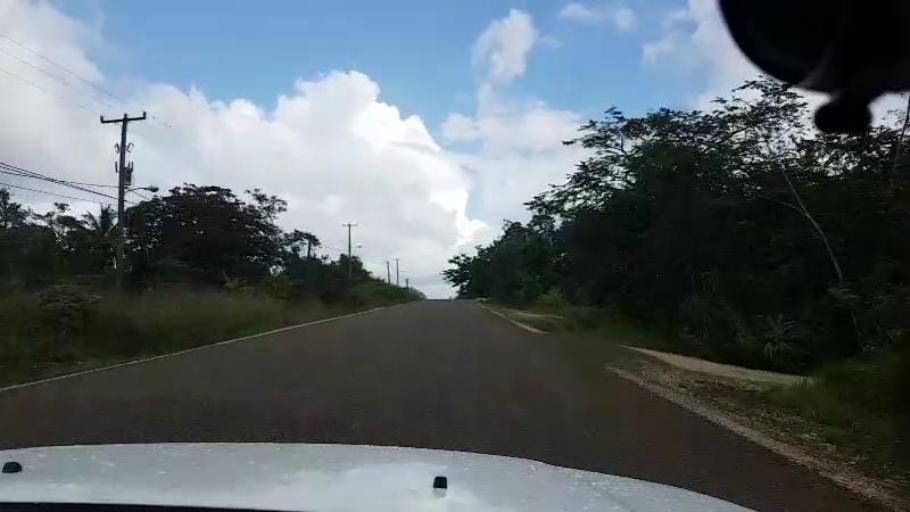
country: BZ
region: Cayo
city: Belmopan
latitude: 17.0919
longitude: -88.6391
